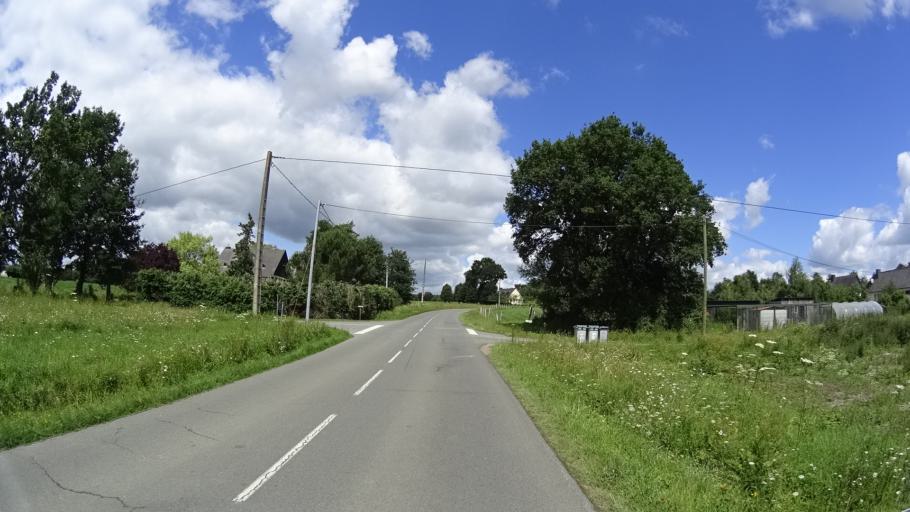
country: FR
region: Brittany
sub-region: Departement d'Ille-et-Vilaine
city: Saint-Gilles
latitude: 48.1371
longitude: -1.8265
